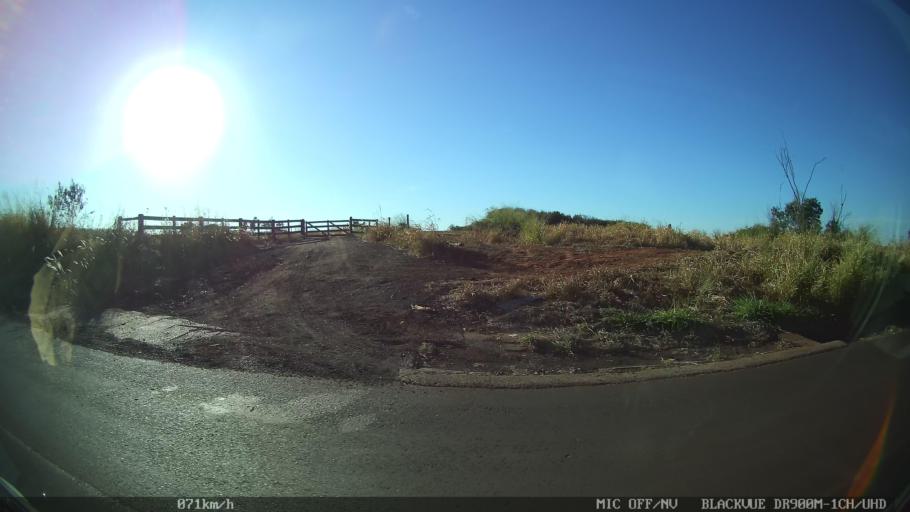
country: BR
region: Sao Paulo
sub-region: Guapiacu
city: Guapiacu
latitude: -20.7709
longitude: -49.2180
